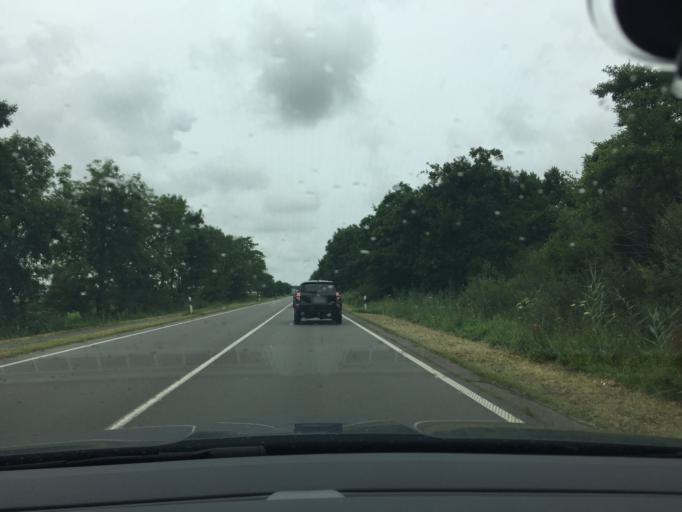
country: DE
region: Lower Saxony
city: Upgant-Schott
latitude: 53.5032
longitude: 7.2962
